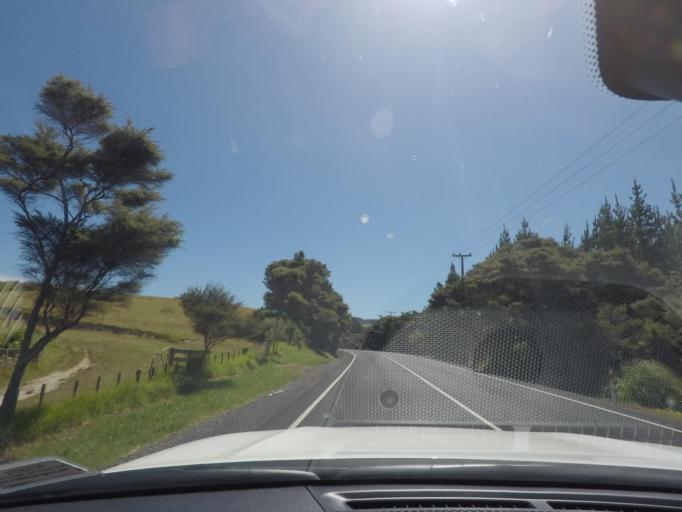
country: NZ
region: Auckland
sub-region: Auckland
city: Parakai
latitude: -36.6250
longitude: 174.3543
